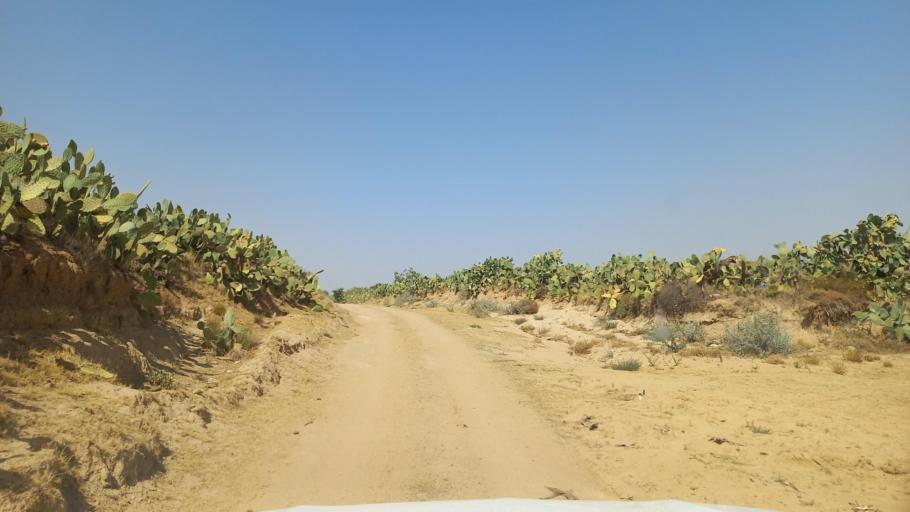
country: TN
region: Al Qasrayn
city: Kasserine
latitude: 35.2430
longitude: 9.0501
